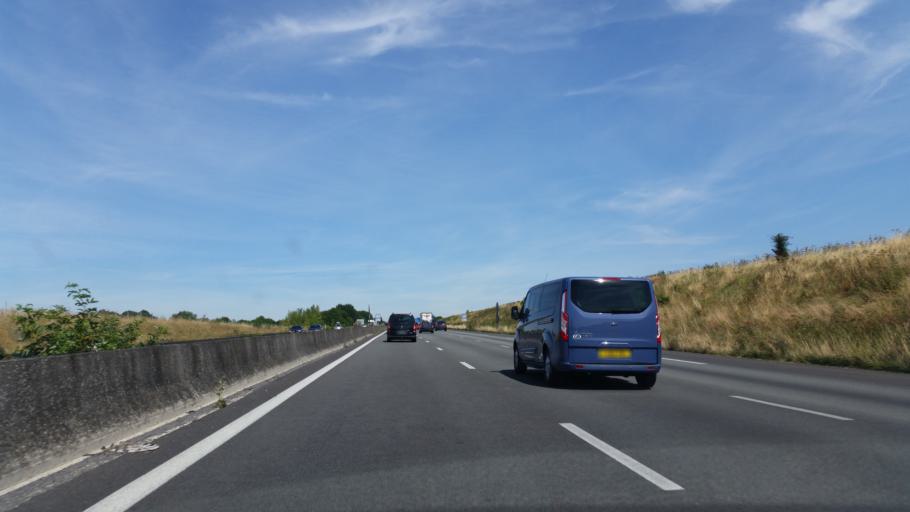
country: FR
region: Picardie
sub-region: Departement de la Somme
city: Peronne
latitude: 49.9750
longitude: 2.8646
